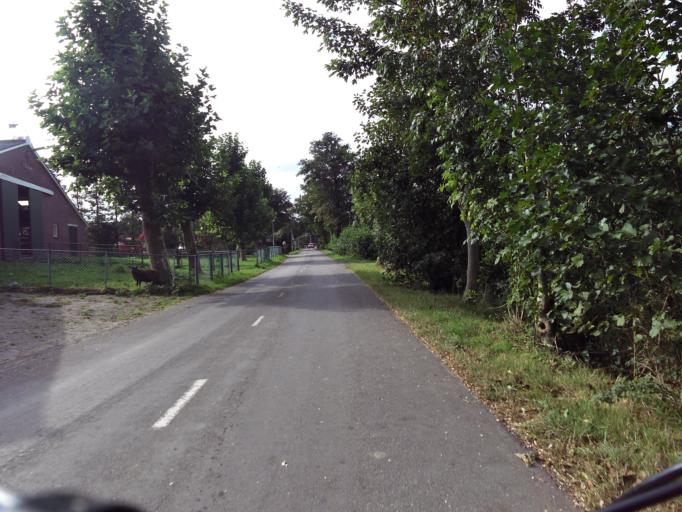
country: NL
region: South Holland
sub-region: Gemeente Rijnwoude
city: Benthuizen
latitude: 52.1054
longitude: 4.5174
